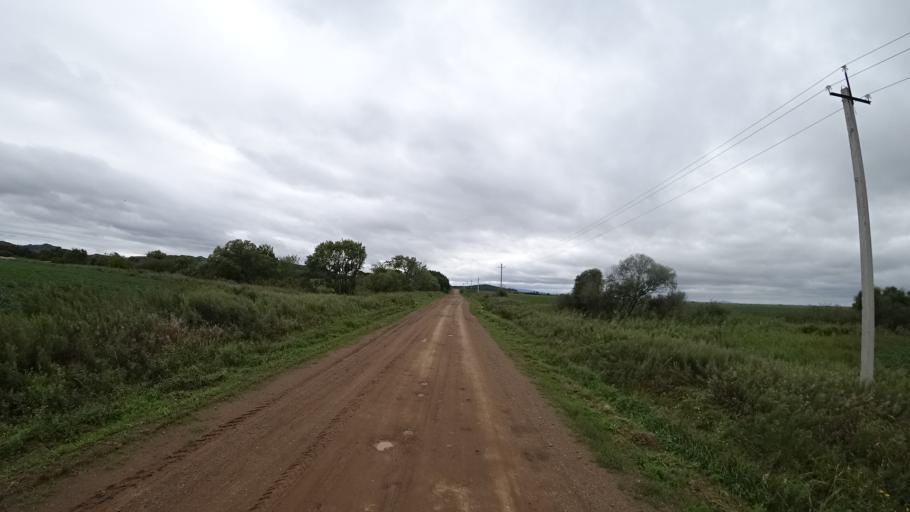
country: RU
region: Primorskiy
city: Chernigovka
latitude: 44.4884
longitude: 132.5727
